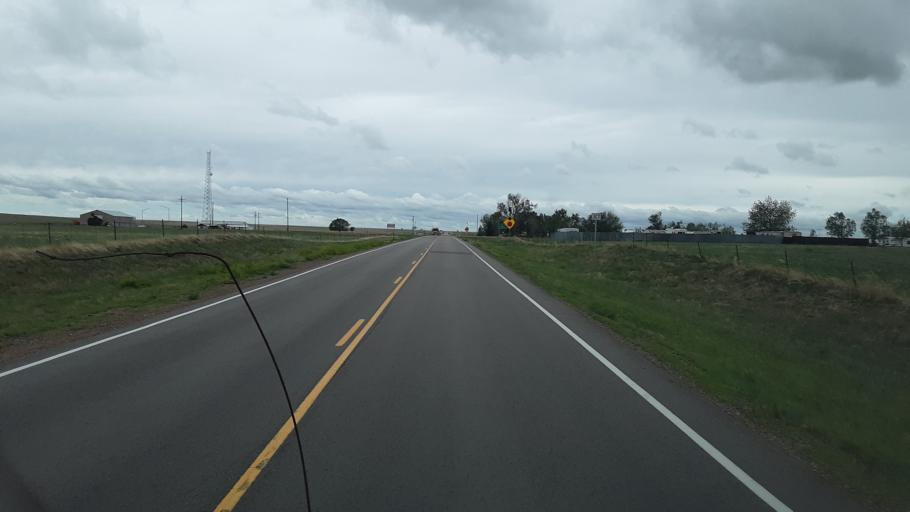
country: US
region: Colorado
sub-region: Lincoln County
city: Hugo
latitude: 38.8519
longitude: -103.6971
